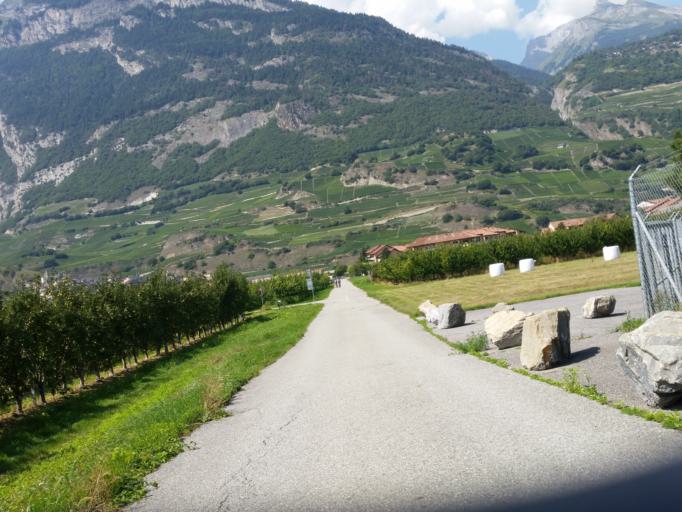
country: CH
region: Valais
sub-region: Martigny District
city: Saillon
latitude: 46.1692
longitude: 7.1987
